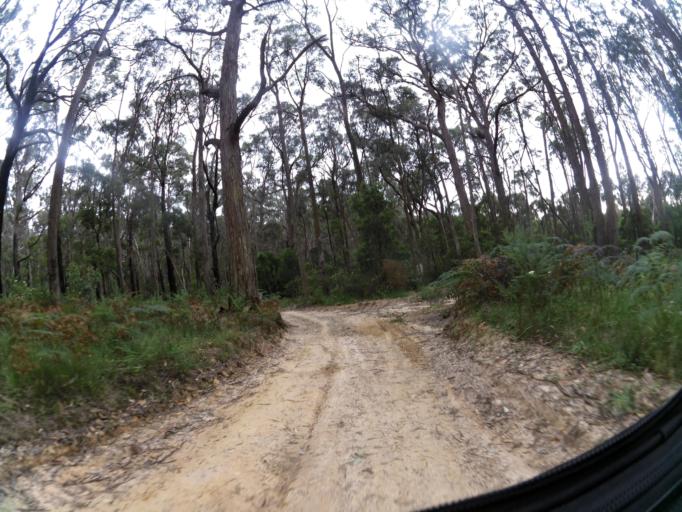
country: AU
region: Victoria
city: Brown Hill
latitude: -37.5187
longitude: 143.9119
